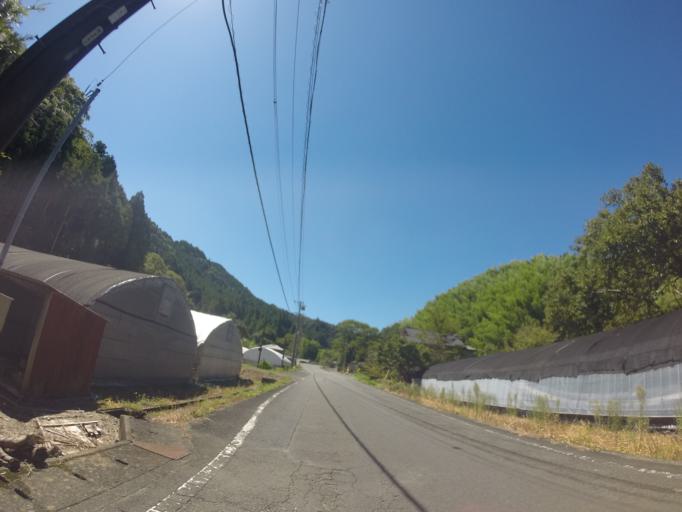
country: JP
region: Shizuoka
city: Fujieda
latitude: 34.9145
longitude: 138.1842
